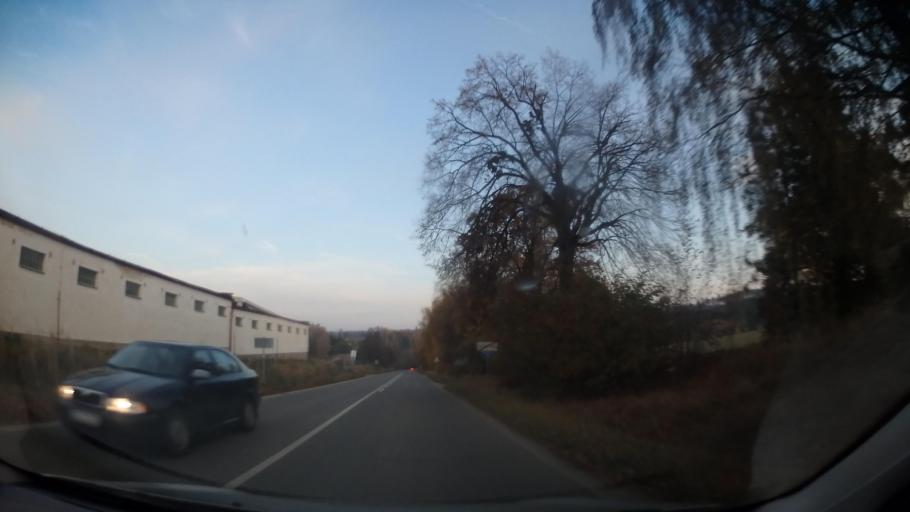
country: CZ
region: Central Bohemia
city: Cechtice
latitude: 49.5554
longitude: 15.1211
